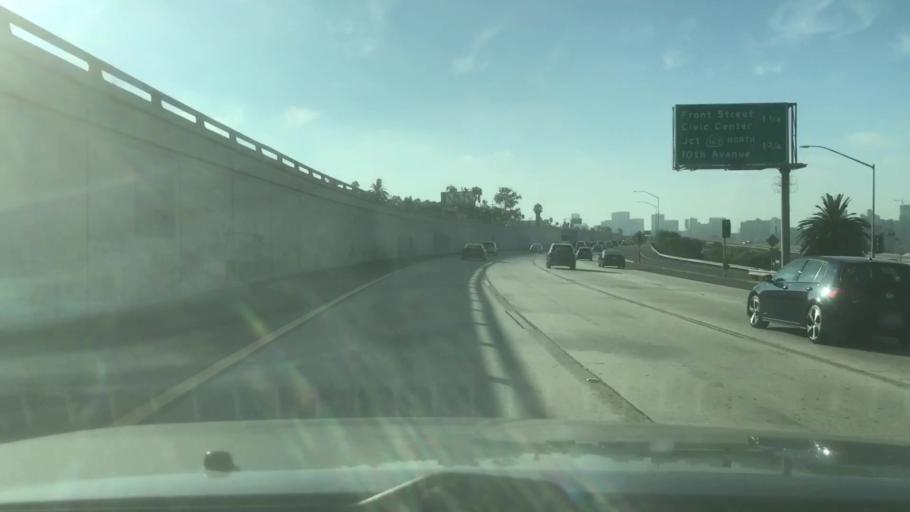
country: US
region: California
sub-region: San Diego County
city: San Diego
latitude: 32.7421
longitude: -117.1806
